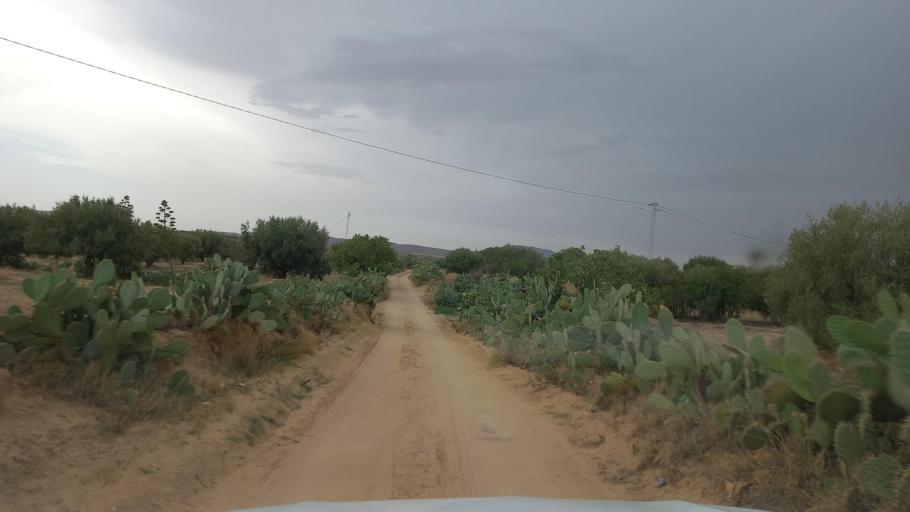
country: TN
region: Al Qasrayn
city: Kasserine
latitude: 35.2408
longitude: 9.0251
